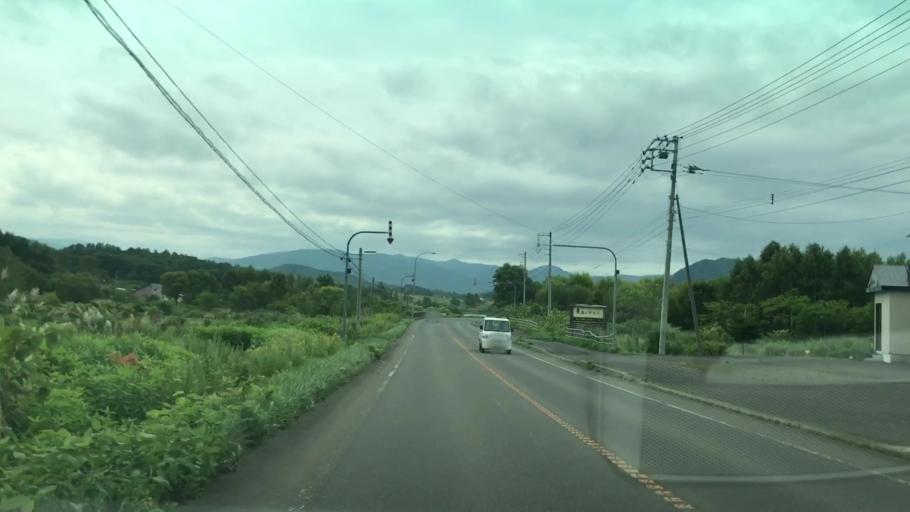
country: JP
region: Hokkaido
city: Yoichi
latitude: 43.1011
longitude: 140.8237
